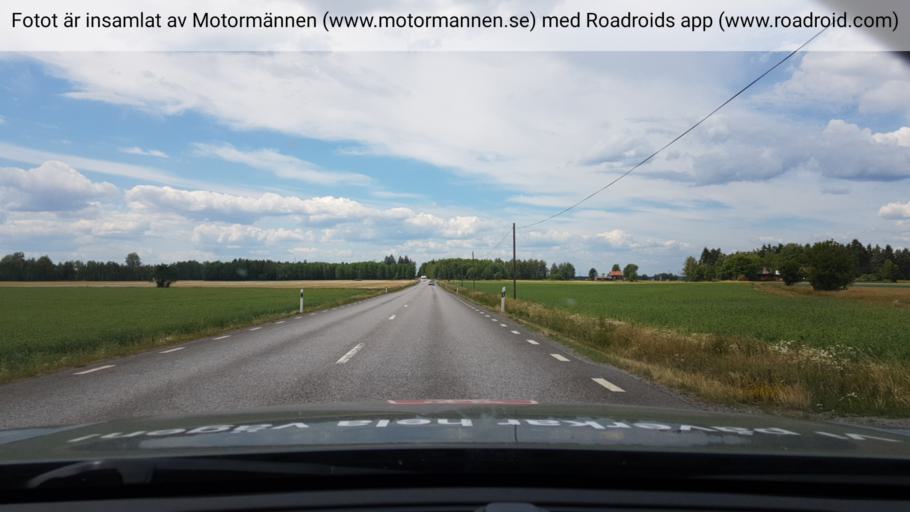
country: SE
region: Vaestmanland
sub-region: Sala Kommun
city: Sala
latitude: 59.8464
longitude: 16.6661
